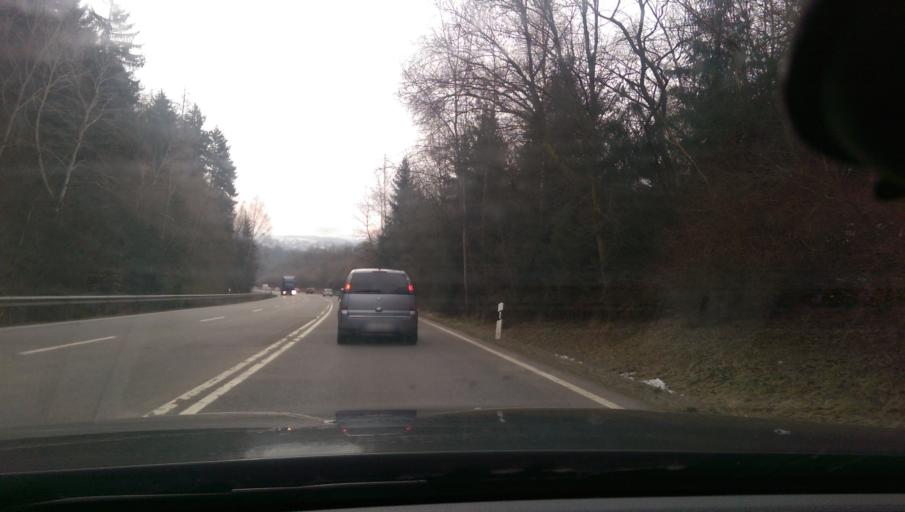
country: DE
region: Bavaria
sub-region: Lower Bavaria
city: Passau
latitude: 48.5823
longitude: 13.4200
